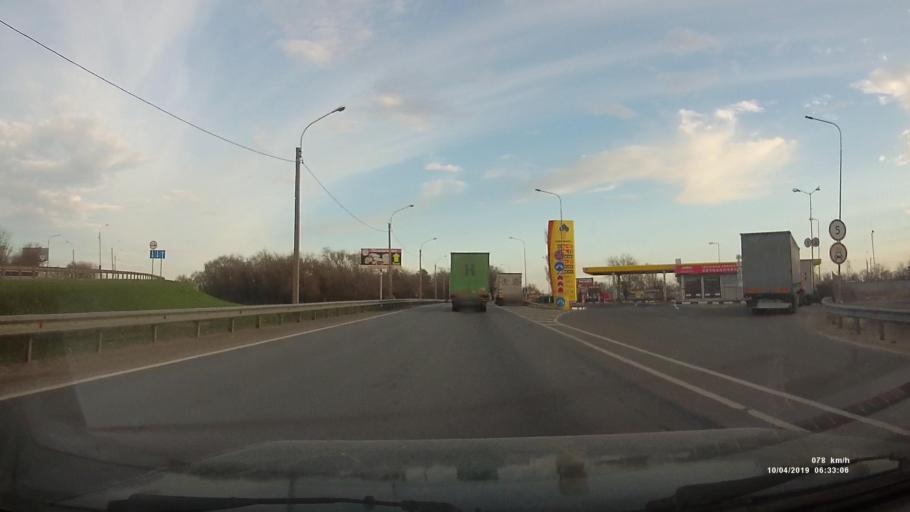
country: RU
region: Rostov
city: Aksay
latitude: 47.2824
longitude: 39.8504
